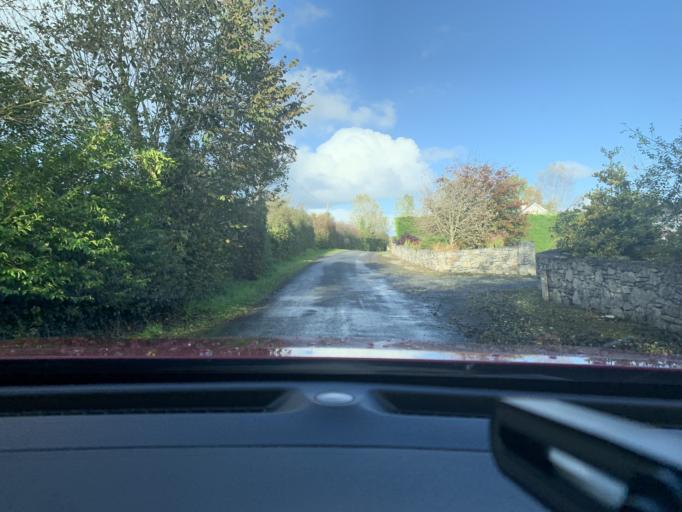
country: IE
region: Connaught
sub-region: Sligo
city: Ballymote
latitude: 54.1072
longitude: -8.4337
